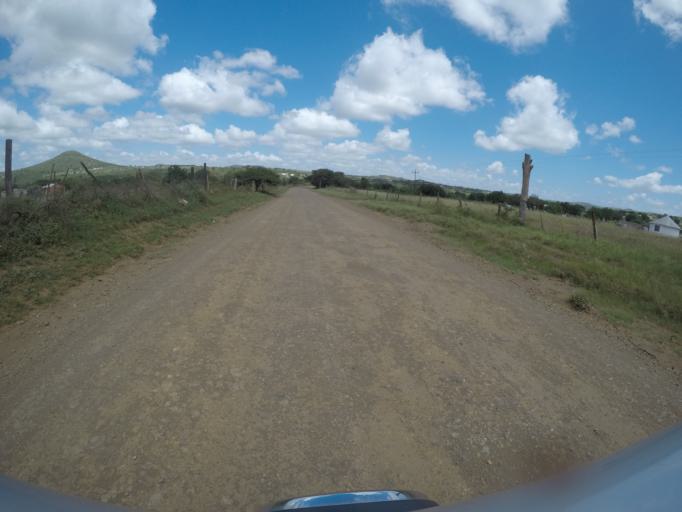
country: ZA
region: KwaZulu-Natal
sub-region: uThungulu District Municipality
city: Empangeni
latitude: -28.5856
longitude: 31.8453
